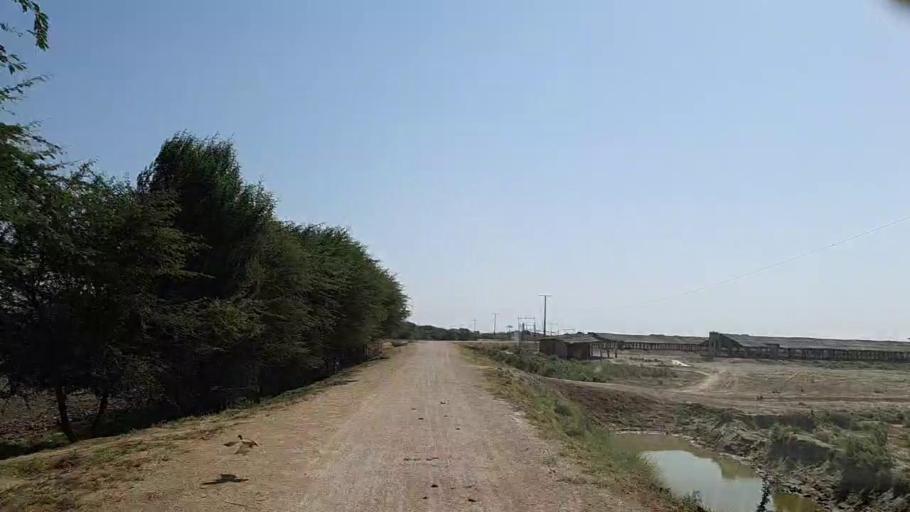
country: PK
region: Sindh
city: Mirpur Batoro
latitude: 24.6797
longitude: 68.2999
